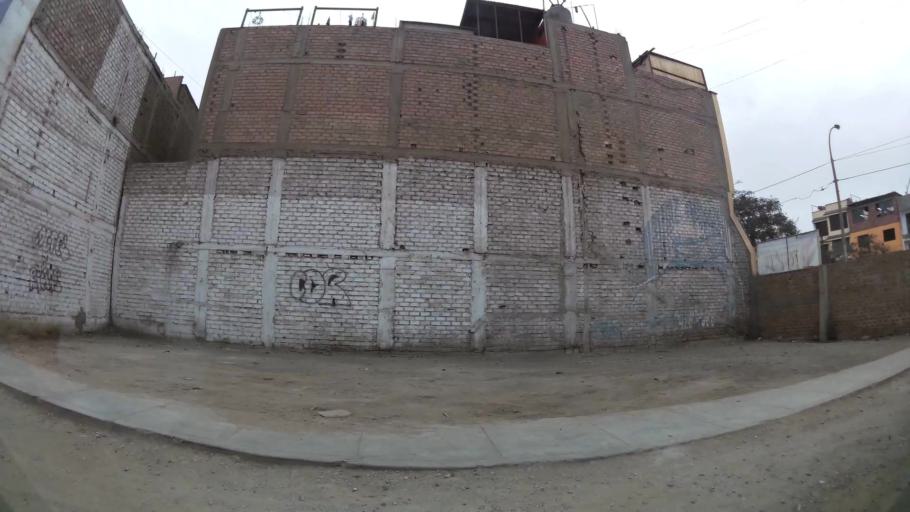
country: PE
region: Lima
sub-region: Lima
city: Independencia
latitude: -11.9607
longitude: -77.0607
